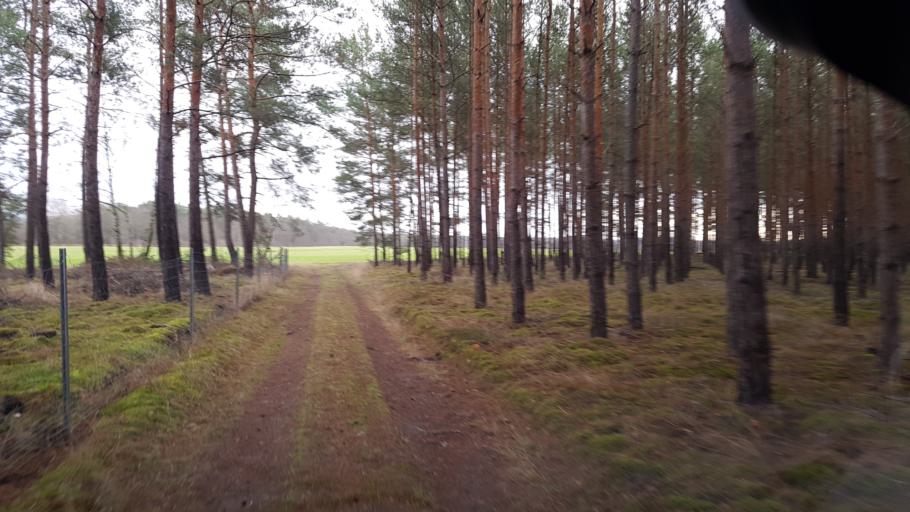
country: DE
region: Brandenburg
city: Altdobern
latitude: 51.6780
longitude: 14.0253
